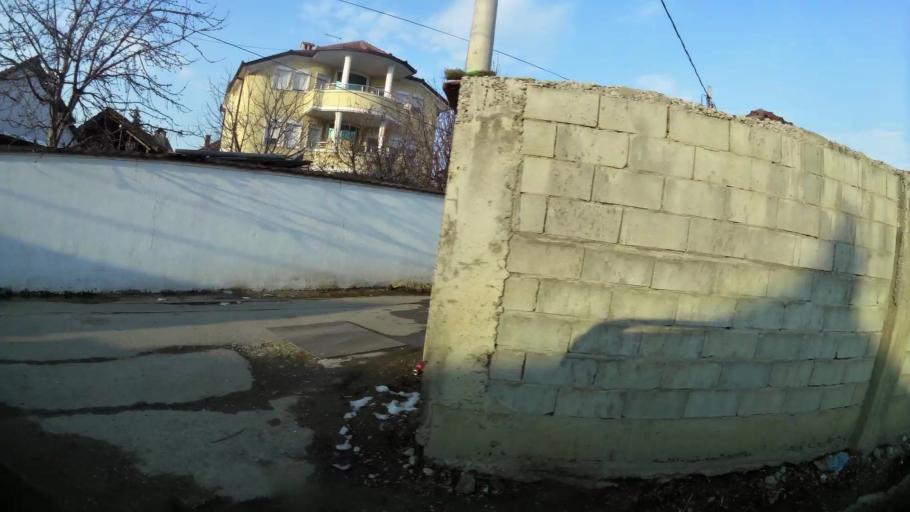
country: MK
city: Creshevo
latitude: 42.0185
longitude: 21.5189
